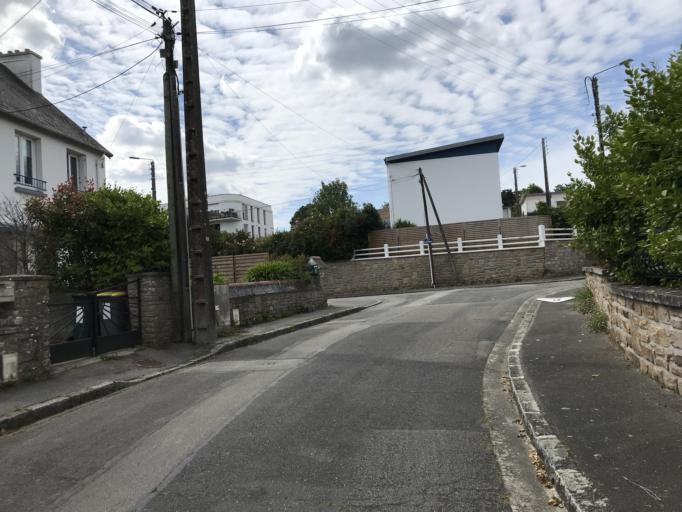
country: FR
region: Brittany
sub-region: Departement du Finistere
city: Brest
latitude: 48.3955
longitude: -4.4405
